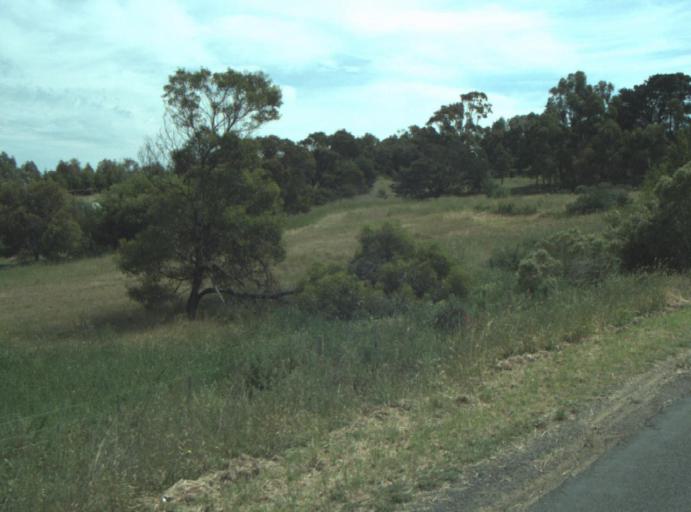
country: AU
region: Victoria
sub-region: Greater Geelong
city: Clifton Springs
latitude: -38.1538
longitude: 144.5898
